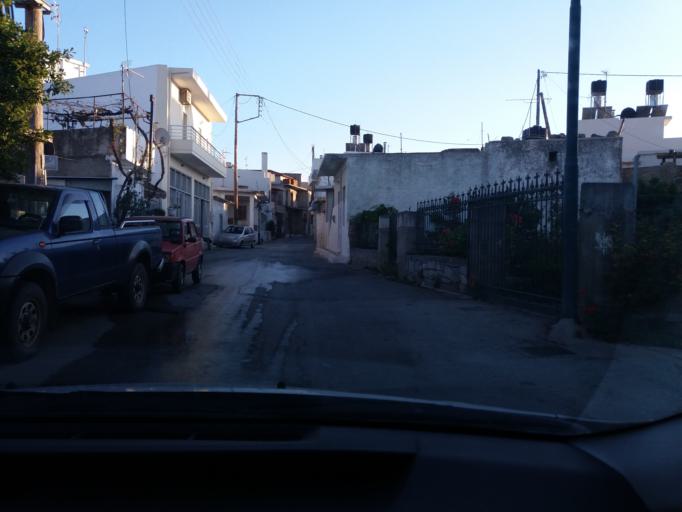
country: GR
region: Crete
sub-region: Nomos Irakleiou
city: Mokhos
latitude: 35.2649
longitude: 25.4230
